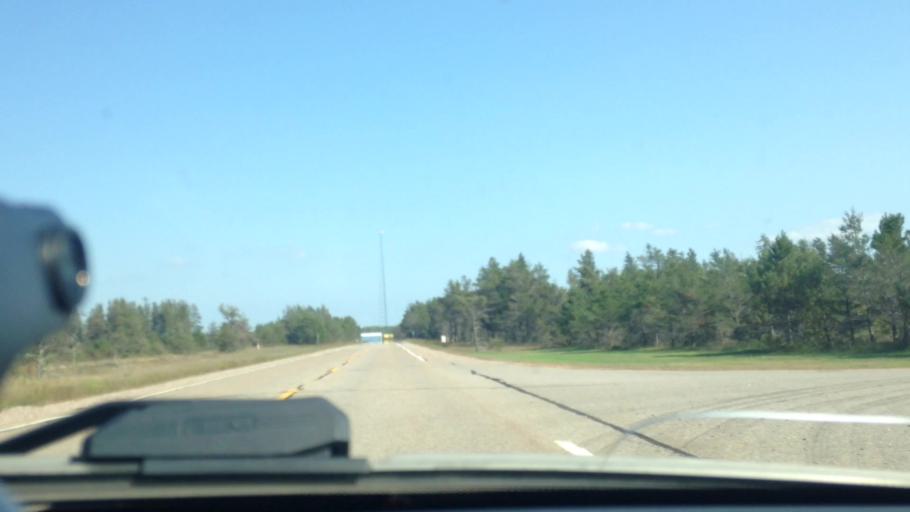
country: US
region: Michigan
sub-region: Chippewa County
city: Sault Ste. Marie
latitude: 46.3589
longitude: -84.8048
